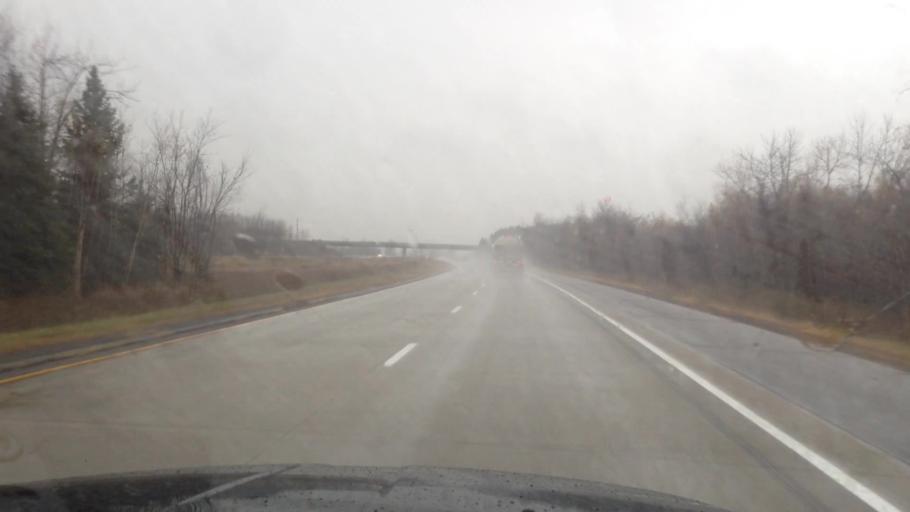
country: CA
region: Ontario
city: Hawkesbury
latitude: 45.4039
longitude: -74.7716
